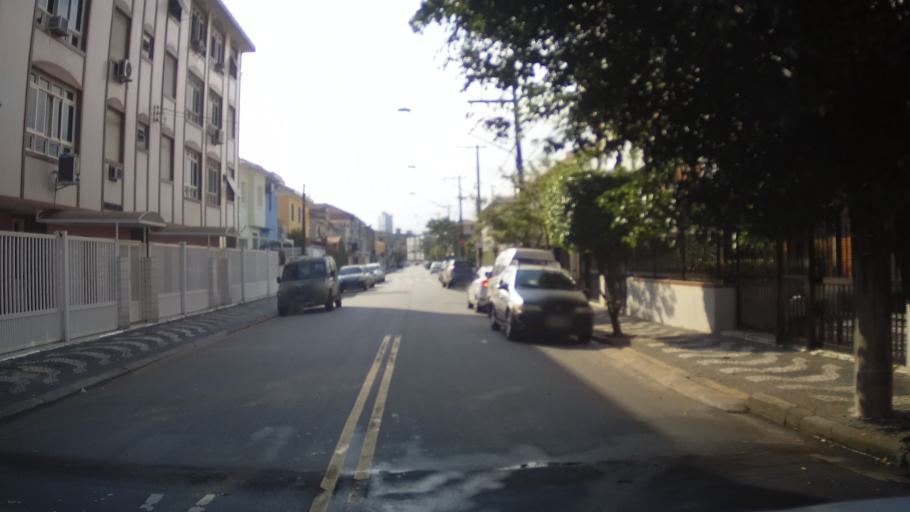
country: BR
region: Sao Paulo
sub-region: Santos
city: Santos
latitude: -23.9787
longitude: -46.3042
